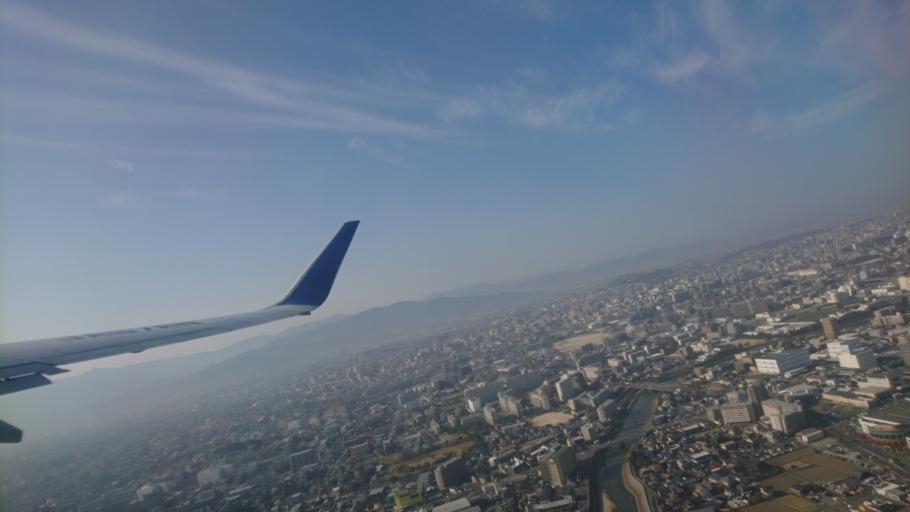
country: JP
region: Fukuoka
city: Onojo
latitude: 33.5704
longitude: 130.4627
